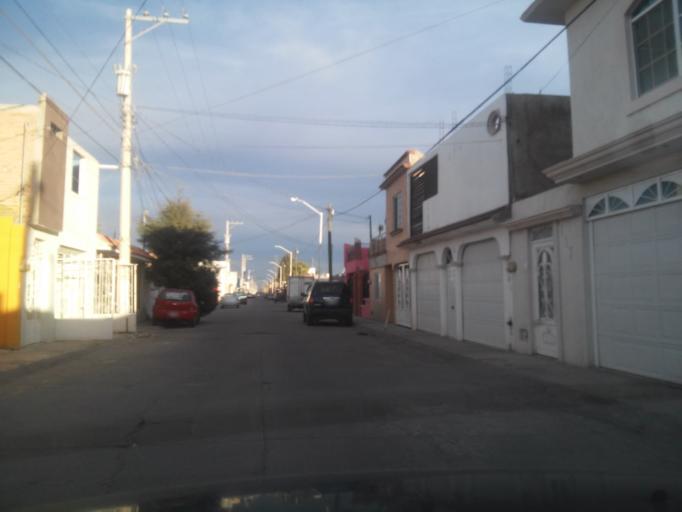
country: MX
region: Durango
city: Victoria de Durango
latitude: 24.0031
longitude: -104.6357
